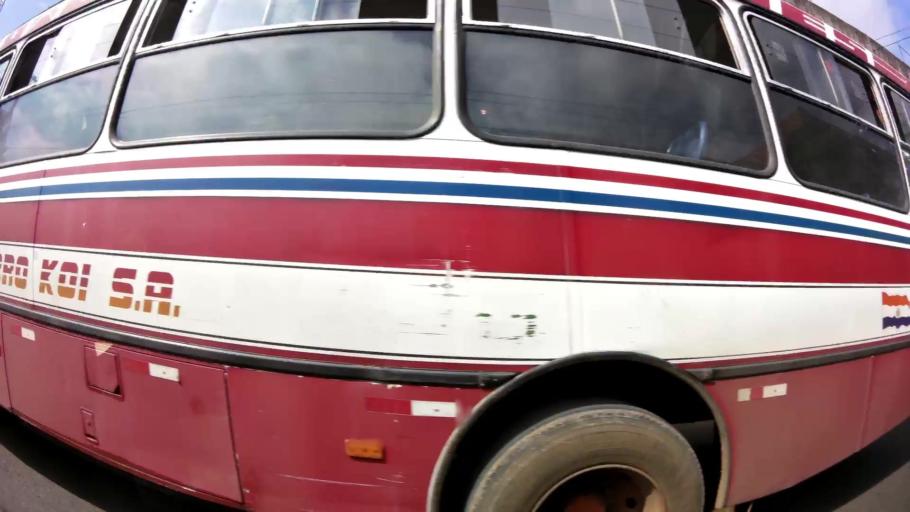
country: PY
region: Central
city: San Lorenzo
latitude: -25.2714
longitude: -57.4927
